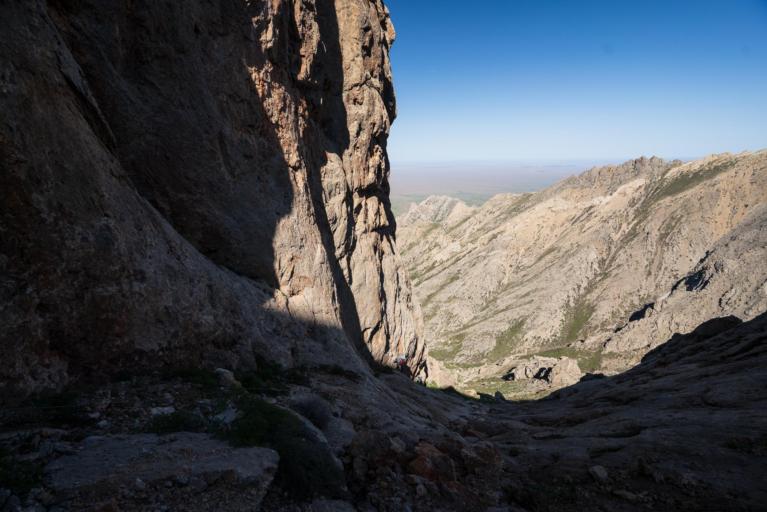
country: KZ
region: Ongtustik Qazaqstan
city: Ashchysay
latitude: 43.7628
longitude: 68.7845
